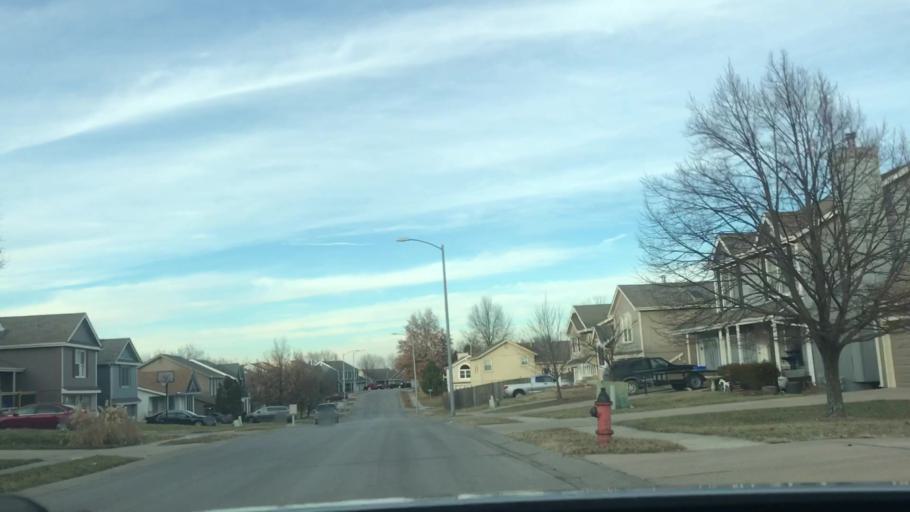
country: US
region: Missouri
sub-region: Platte County
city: Riverside
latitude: 39.2042
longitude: -94.5965
